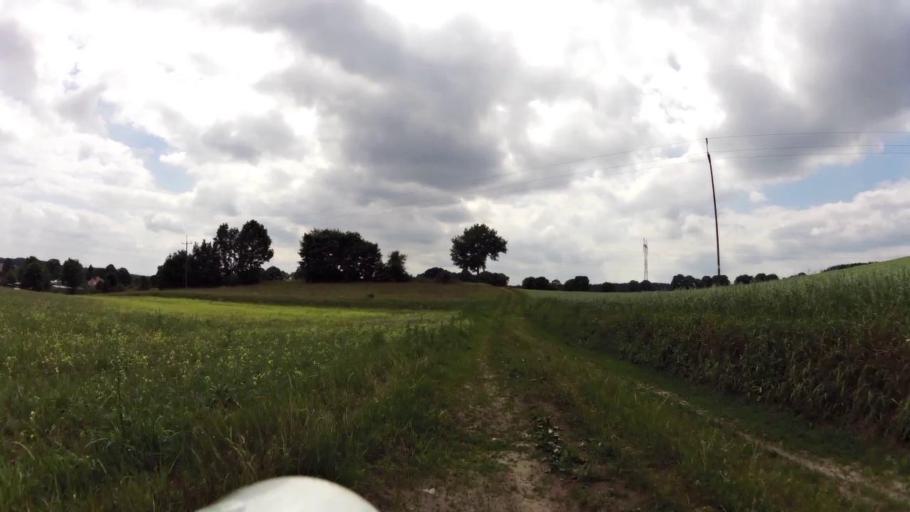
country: PL
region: West Pomeranian Voivodeship
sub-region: Powiat szczecinecki
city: Bialy Bor
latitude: 53.9515
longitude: 16.7746
